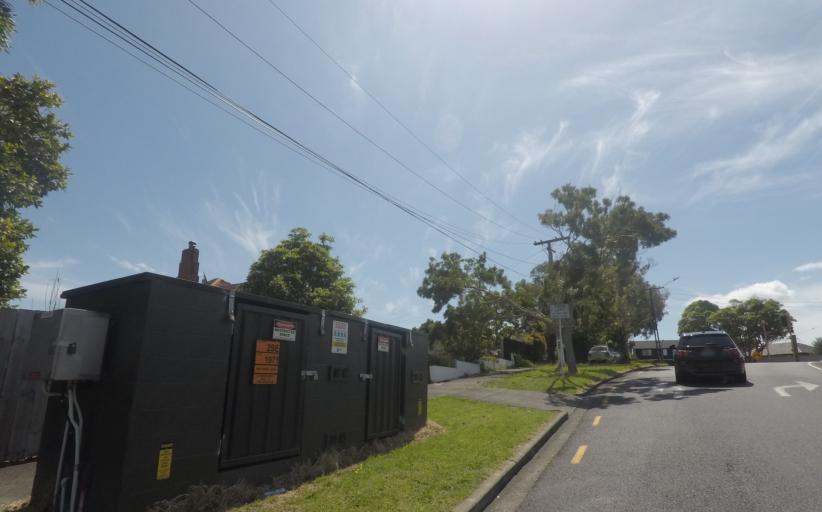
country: NZ
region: Auckland
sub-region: Auckland
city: Tamaki
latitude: -36.8683
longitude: 174.8485
